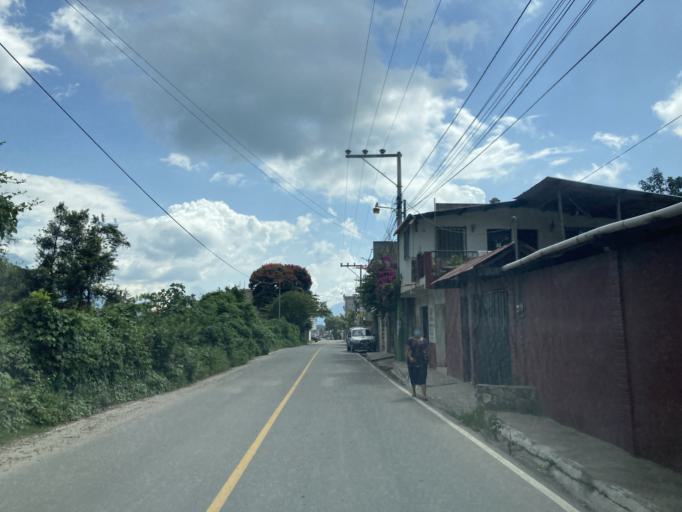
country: GT
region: Solola
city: Panajachel
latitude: 14.7449
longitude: -91.1484
